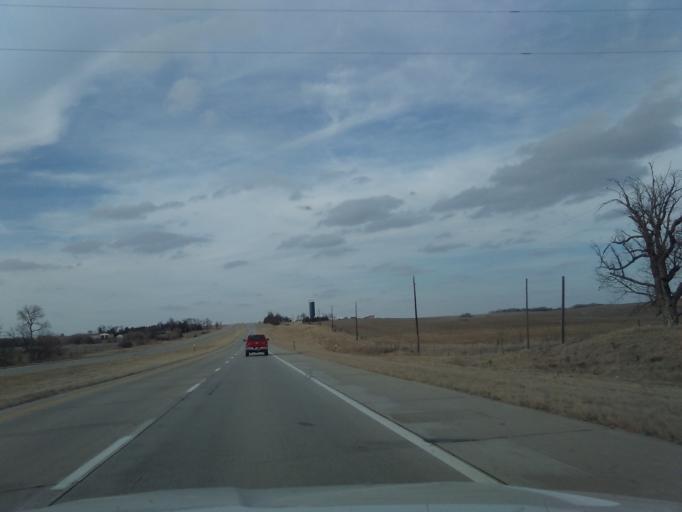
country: US
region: Nebraska
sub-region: Gage County
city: Beatrice
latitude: 40.3868
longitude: -96.7424
